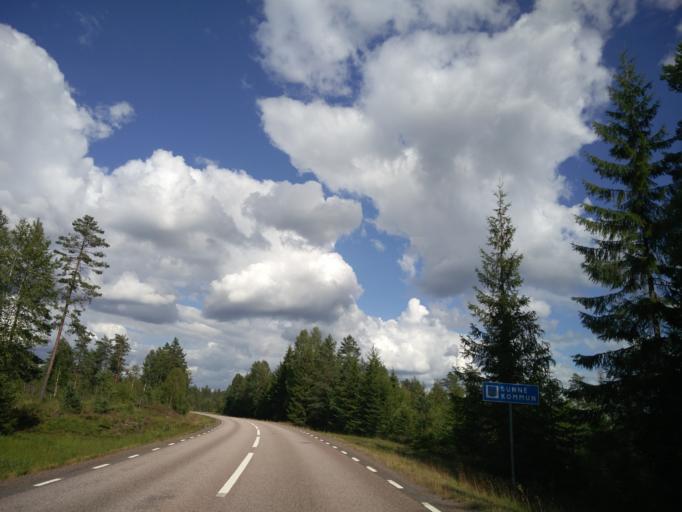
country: SE
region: Vaermland
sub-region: Sunne Kommun
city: Sunne
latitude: 59.6906
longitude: 13.0645
